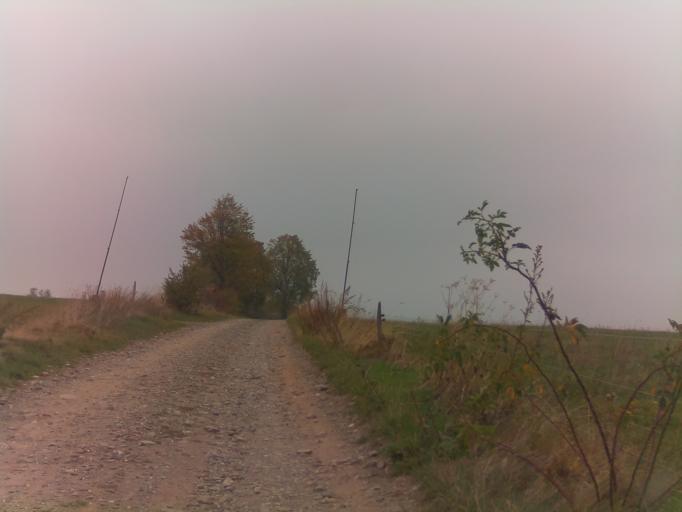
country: DE
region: Thuringia
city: Oberhain
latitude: 50.6371
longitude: 11.1287
